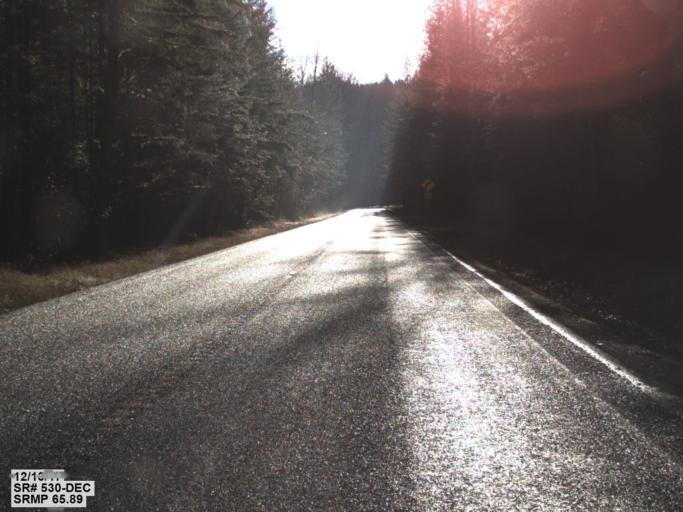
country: US
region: Washington
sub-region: Snohomish County
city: Darrington
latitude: 48.4636
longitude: -121.5863
